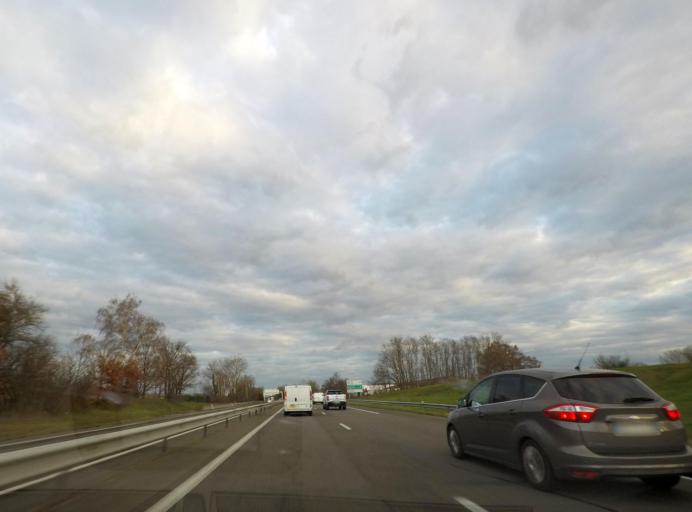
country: FR
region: Rhone-Alpes
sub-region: Departement de l'Ain
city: Crottet
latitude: 46.2912
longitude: 4.9177
